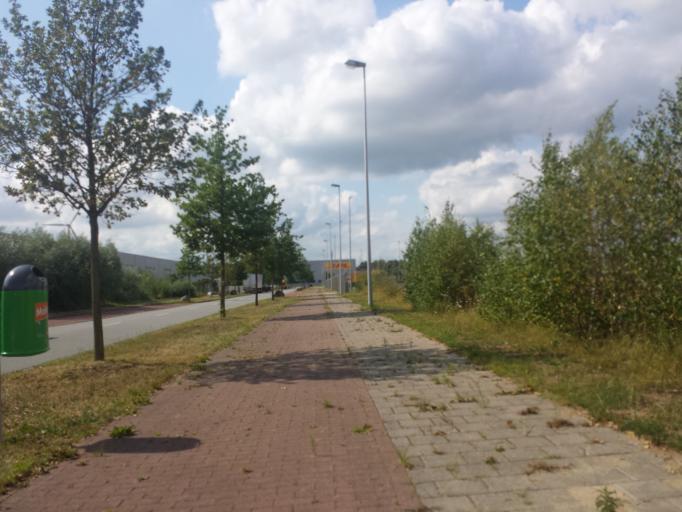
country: DE
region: Lower Saxony
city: Stuhr
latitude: 53.1005
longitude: 8.7106
